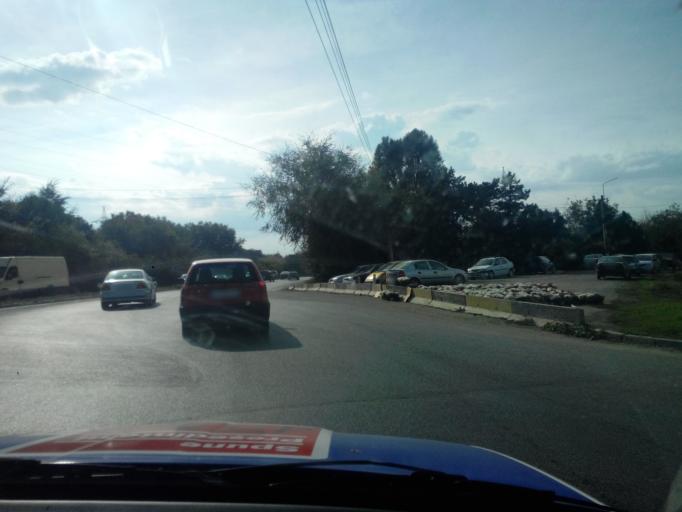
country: RO
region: Constanta
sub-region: Comuna Agigea
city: Agigea
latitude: 44.1317
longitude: 28.6175
